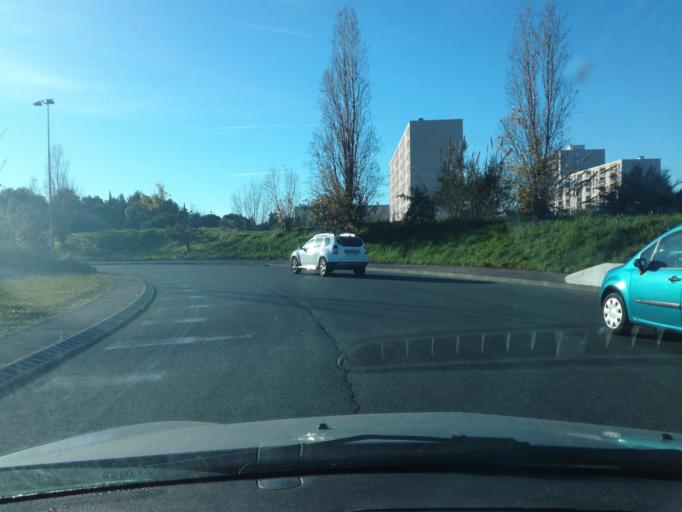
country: FR
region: Provence-Alpes-Cote d'Azur
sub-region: Departement des Alpes-Maritimes
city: Vallauris
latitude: 43.5786
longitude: 7.0901
